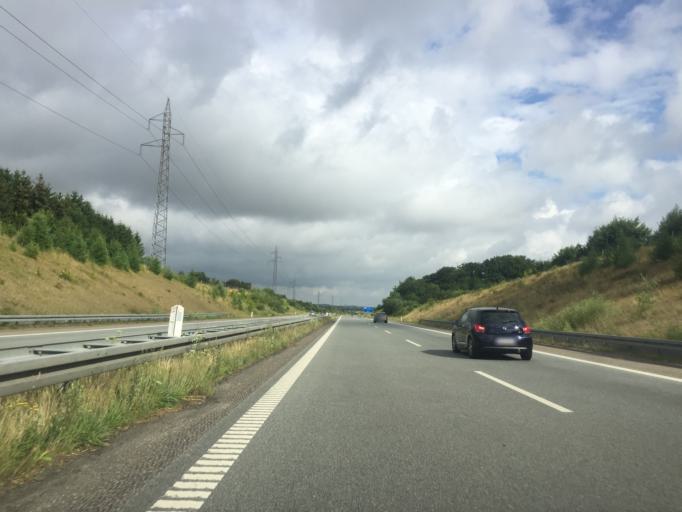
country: DK
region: South Denmark
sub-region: Svendborg Kommune
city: Svendborg
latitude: 55.1017
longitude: 10.5669
